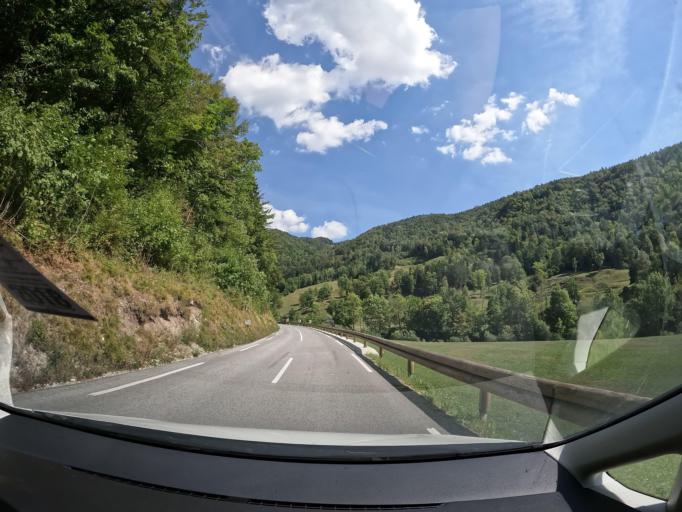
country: SI
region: Preddvor
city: Preddvor
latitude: 46.3005
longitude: 14.4666
